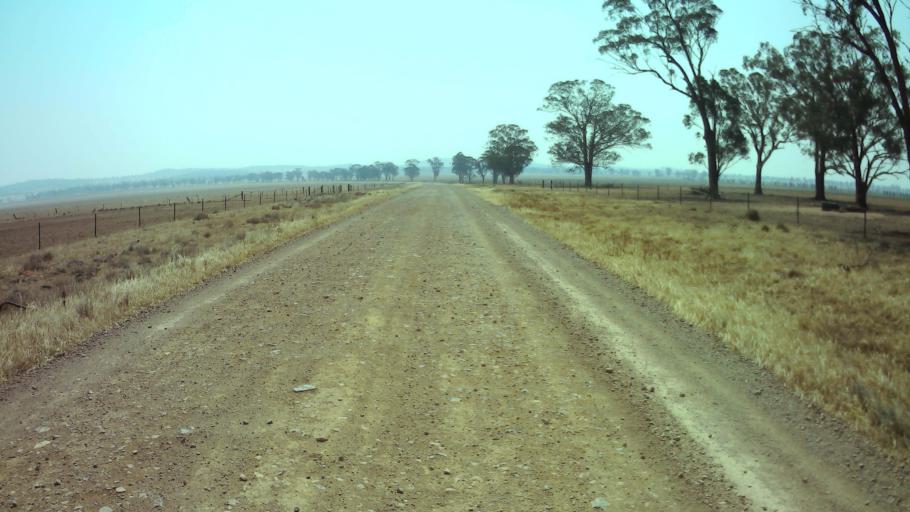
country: AU
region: New South Wales
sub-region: Weddin
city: Grenfell
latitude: -33.6372
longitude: 148.2298
